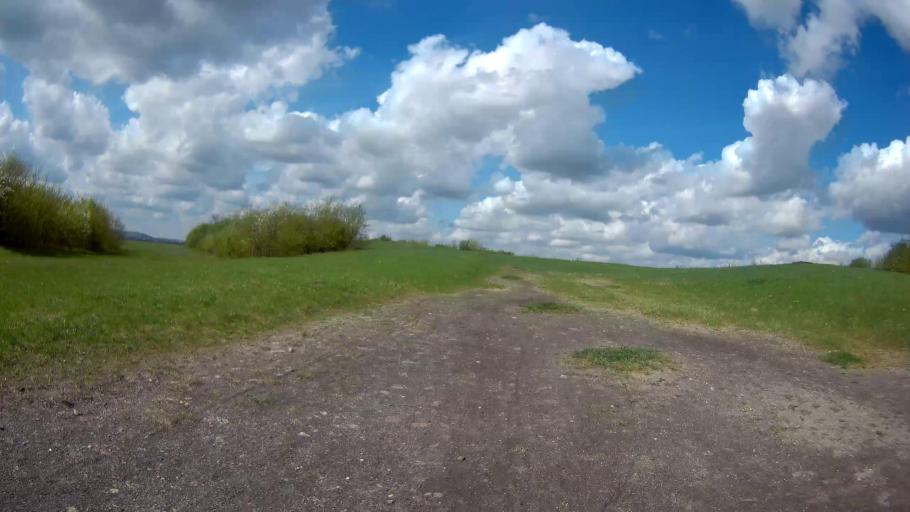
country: DE
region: North Rhine-Westphalia
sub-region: Regierungsbezirk Munster
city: Gladbeck
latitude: 51.5650
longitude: 7.0353
